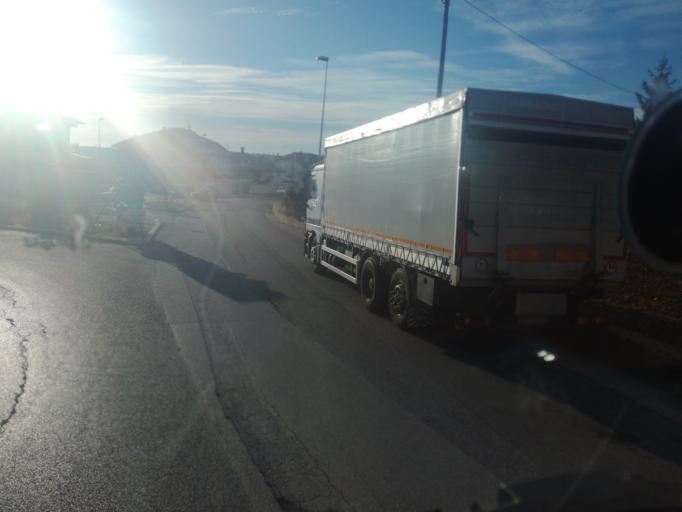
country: IT
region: Abruzzo
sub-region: Provincia di Chieti
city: Francavilla al Mare
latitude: 42.3980
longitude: 14.2936
